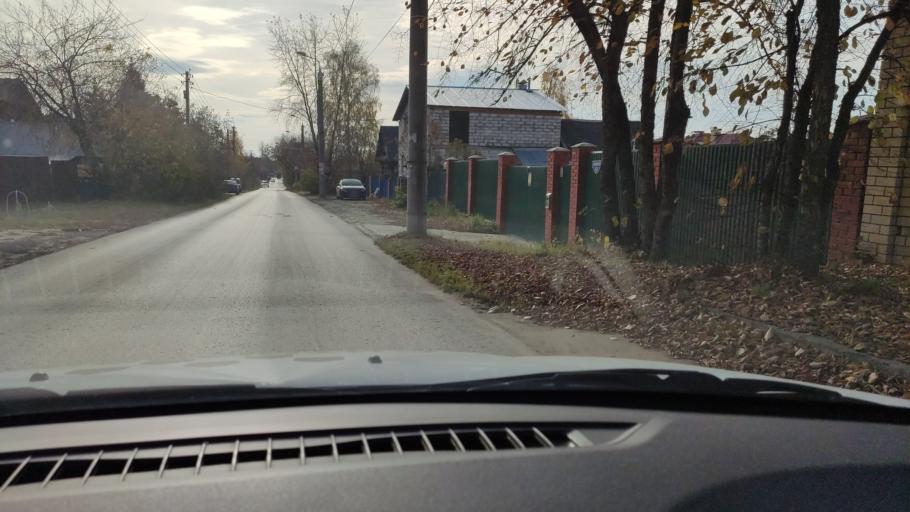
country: RU
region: Perm
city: Kondratovo
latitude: 58.0446
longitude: 56.1193
